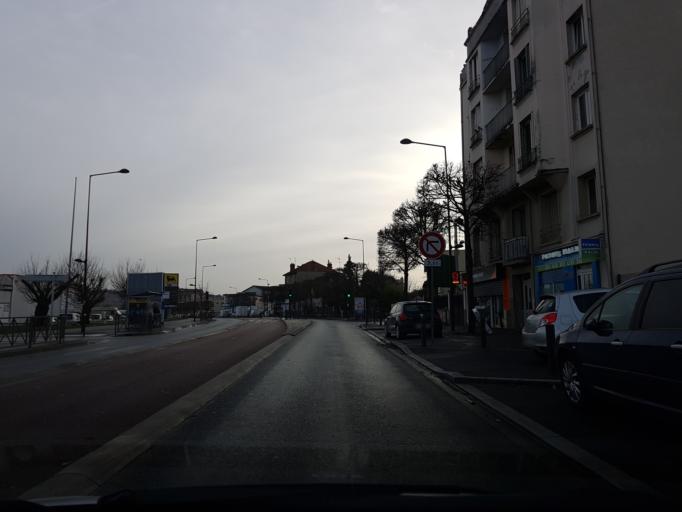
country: FR
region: Ile-de-France
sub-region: Departement du Val-de-Marne
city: Ablon-sur-Seine
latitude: 48.7289
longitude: 2.4302
